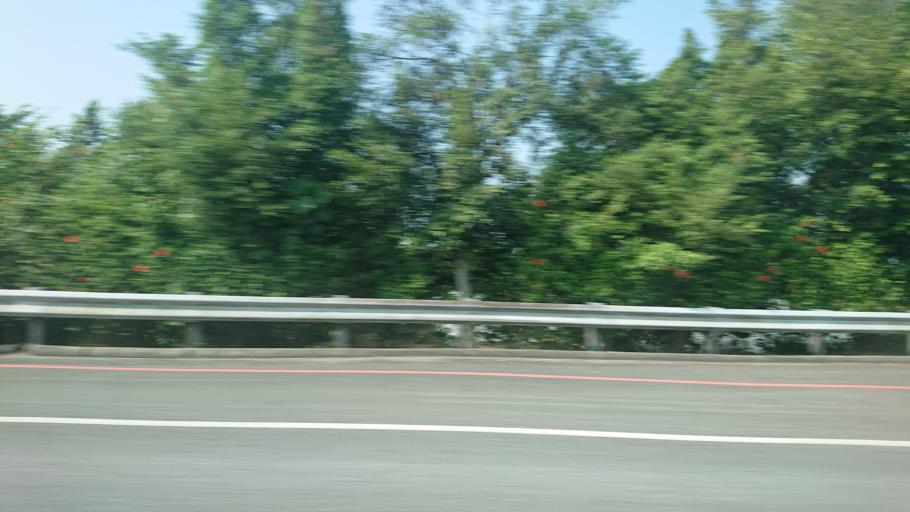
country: TW
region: Taiwan
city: Lugu
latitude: 23.7876
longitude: 120.7046
